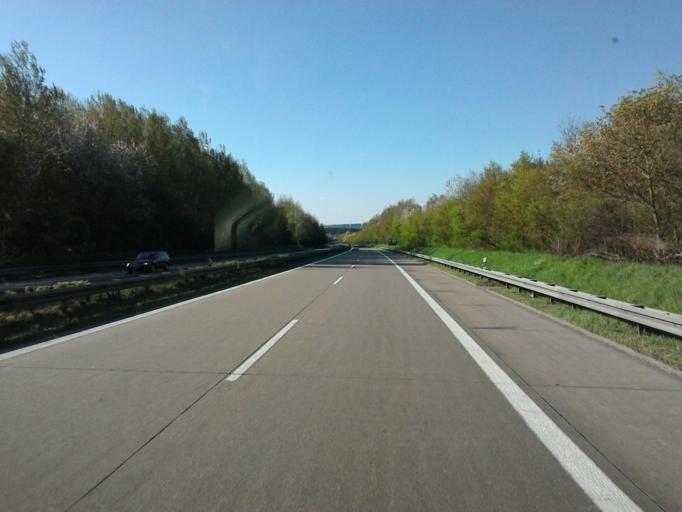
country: DE
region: Baden-Wuerttemberg
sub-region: Regierungsbezirk Stuttgart
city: Nattheim
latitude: 48.7832
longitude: 10.2123
